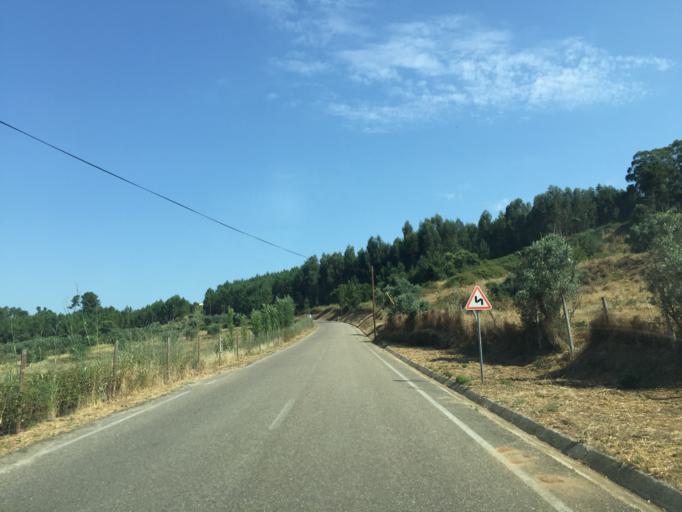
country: PT
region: Santarem
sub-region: Ferreira do Zezere
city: Ferreira do Zezere
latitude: 39.5946
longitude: -8.2987
